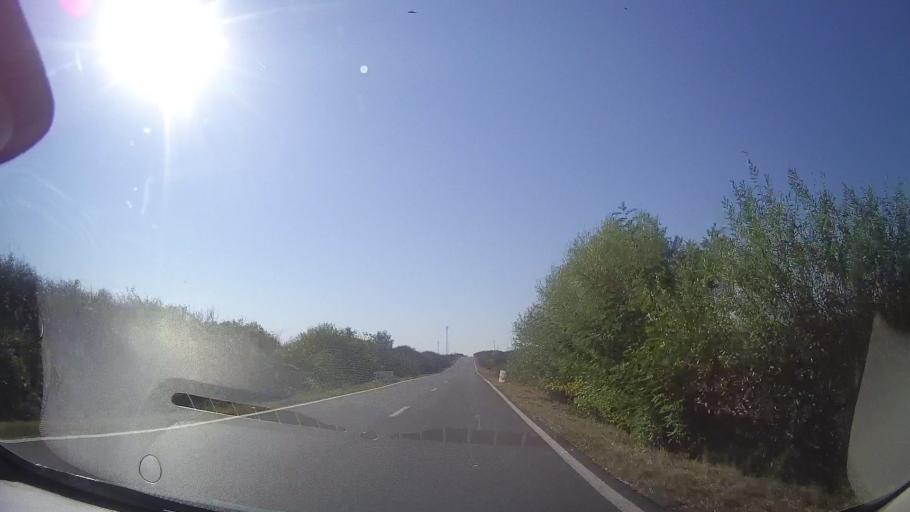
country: RO
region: Timis
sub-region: Comuna Belint
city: Belint
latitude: 45.7703
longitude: 21.7295
